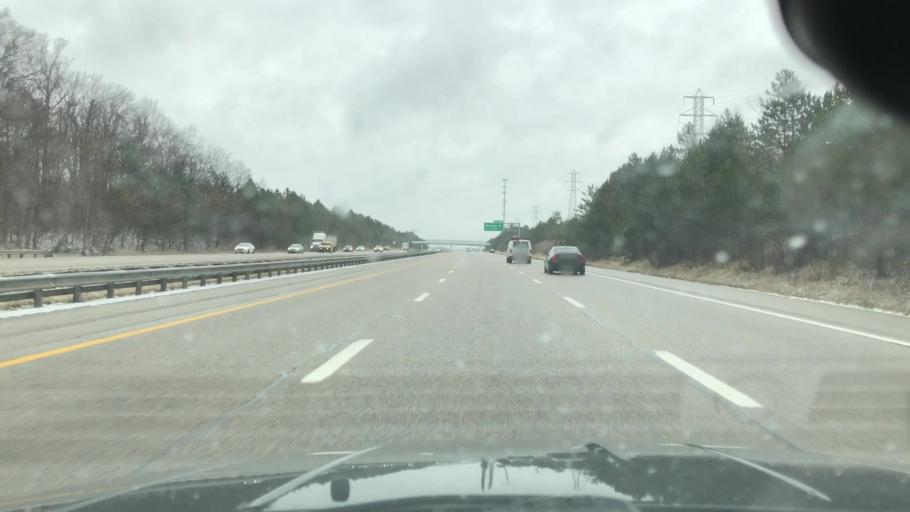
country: US
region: Ohio
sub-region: Cuyahoga County
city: Brecksville
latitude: 41.3306
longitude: -81.6488
